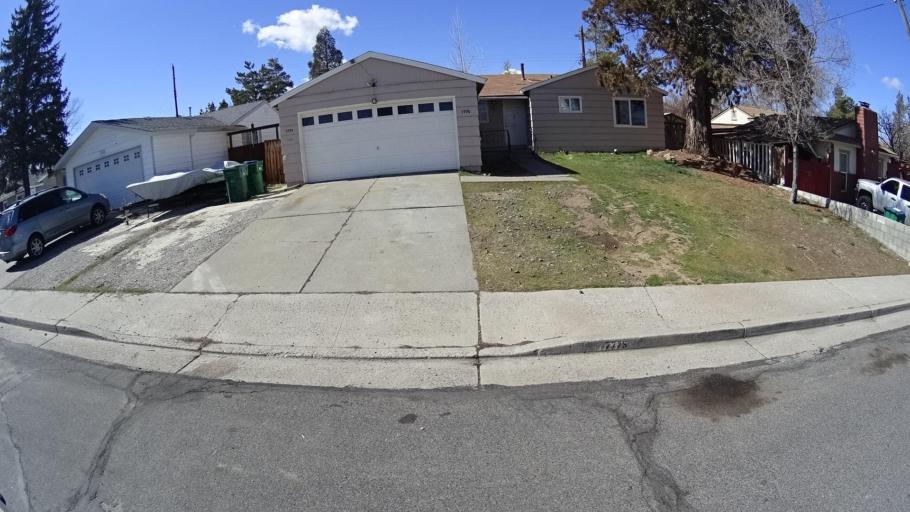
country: US
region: Nevada
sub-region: Washoe County
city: Golden Valley
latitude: 39.5944
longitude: -119.8429
